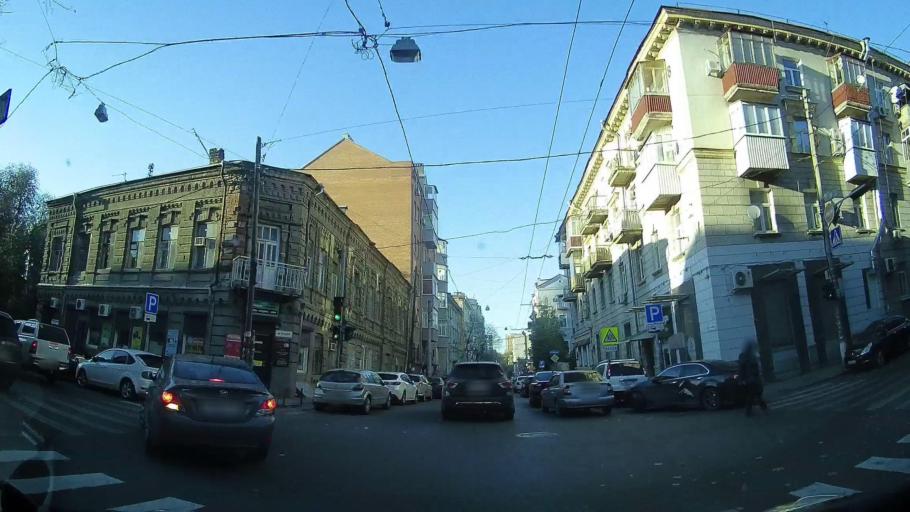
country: RU
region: Rostov
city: Rostov-na-Donu
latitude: 47.2183
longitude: 39.7056
